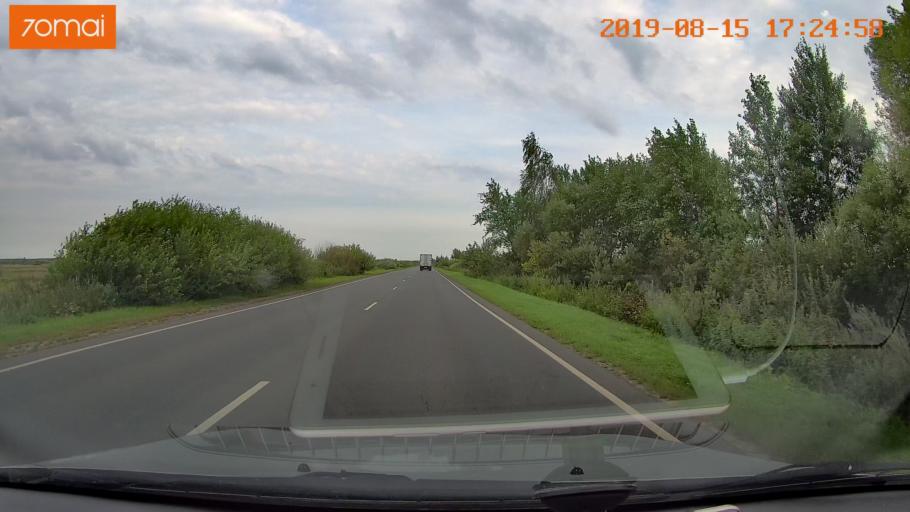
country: RU
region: Moskovskaya
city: Ashitkovo
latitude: 55.3804
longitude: 38.5602
